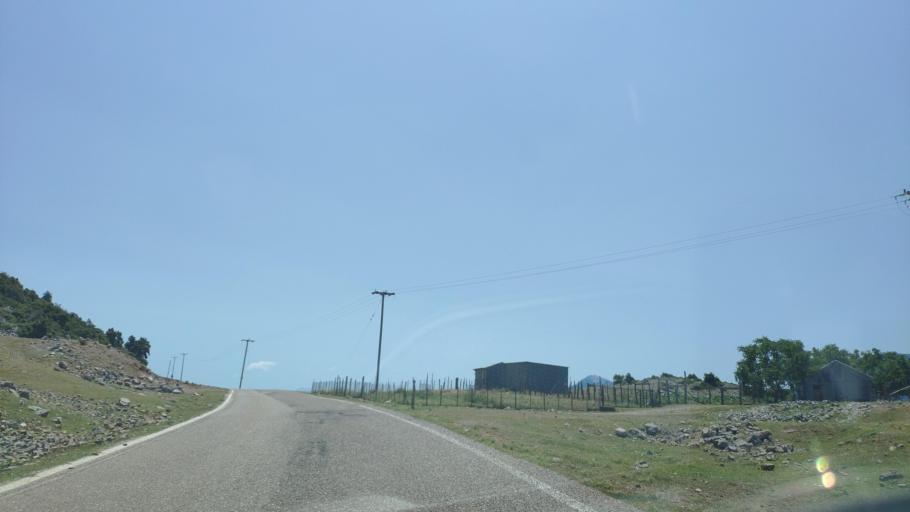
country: GR
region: West Greece
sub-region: Nomos Aitolias kai Akarnanias
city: Krikellos
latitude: 39.0503
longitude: 21.3728
